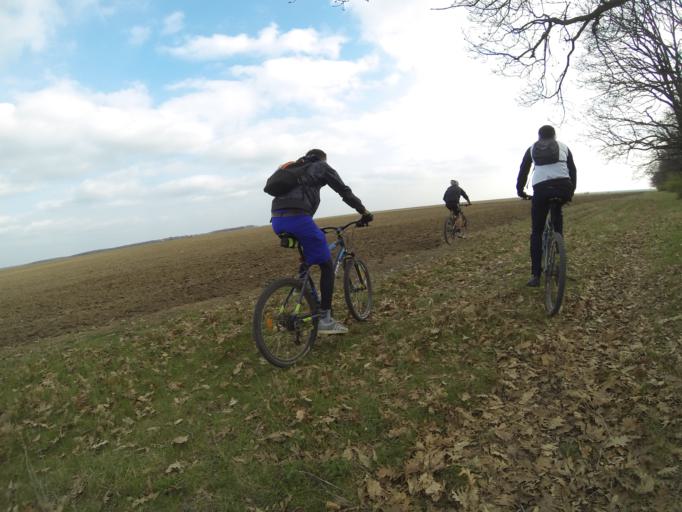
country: RO
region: Dolj
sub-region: Comuna Bucovat
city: Bucovat
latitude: 44.2494
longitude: 23.7083
